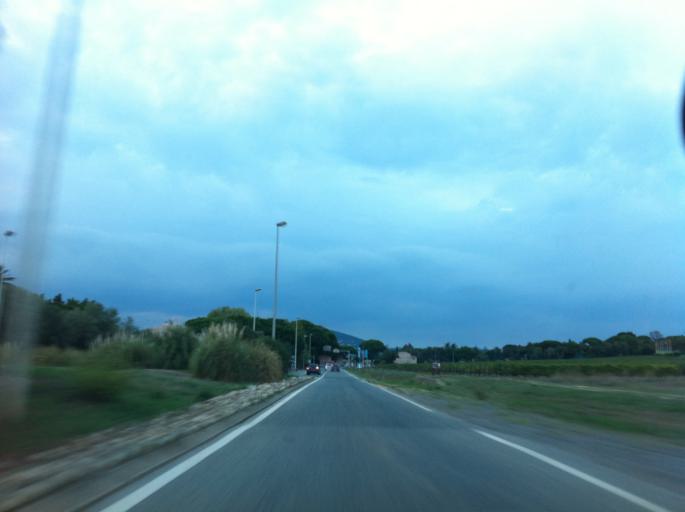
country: FR
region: Provence-Alpes-Cote d'Azur
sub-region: Departement du Var
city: Gassin
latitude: 43.2568
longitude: 6.5946
